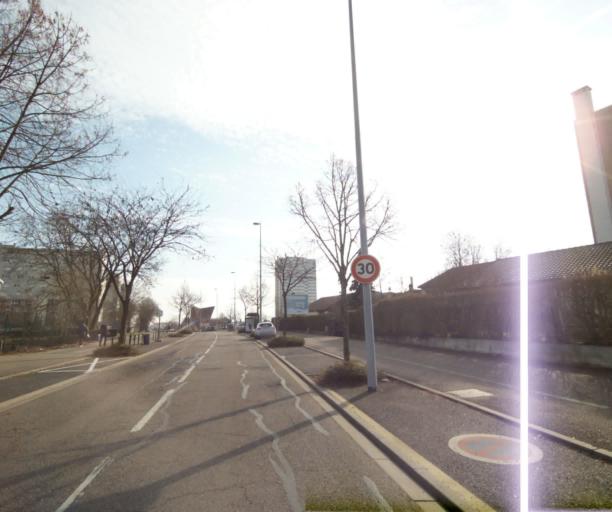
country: FR
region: Lorraine
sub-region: Departement de Meurthe-et-Moselle
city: Laxou
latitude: 48.6794
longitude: 6.1438
